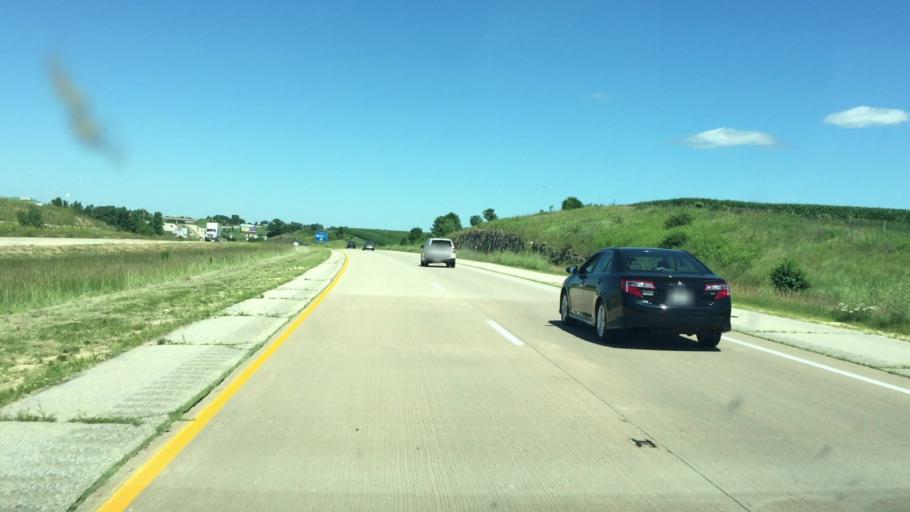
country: US
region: Wisconsin
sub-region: Grant County
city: Platteville
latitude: 42.7390
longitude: -90.3545
